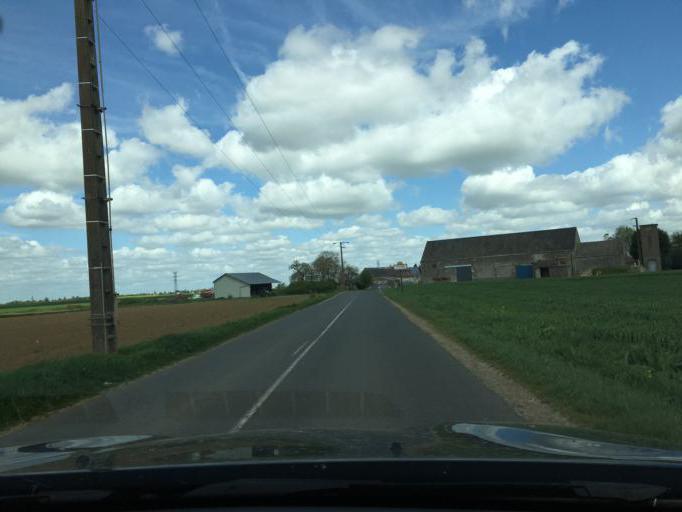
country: FR
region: Centre
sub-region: Departement du Loiret
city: Bricy
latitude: 48.0337
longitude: 1.8013
